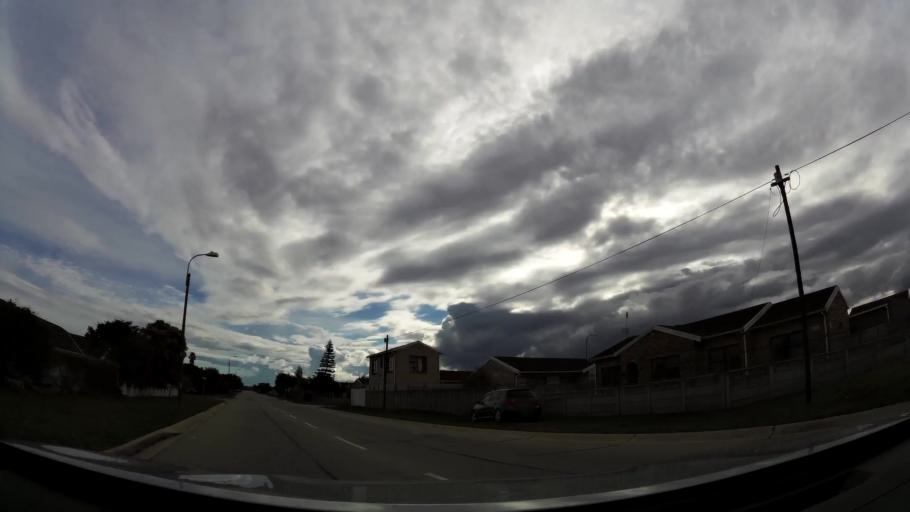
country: ZA
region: Eastern Cape
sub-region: Nelson Mandela Bay Metropolitan Municipality
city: Port Elizabeth
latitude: -33.9423
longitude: 25.4856
